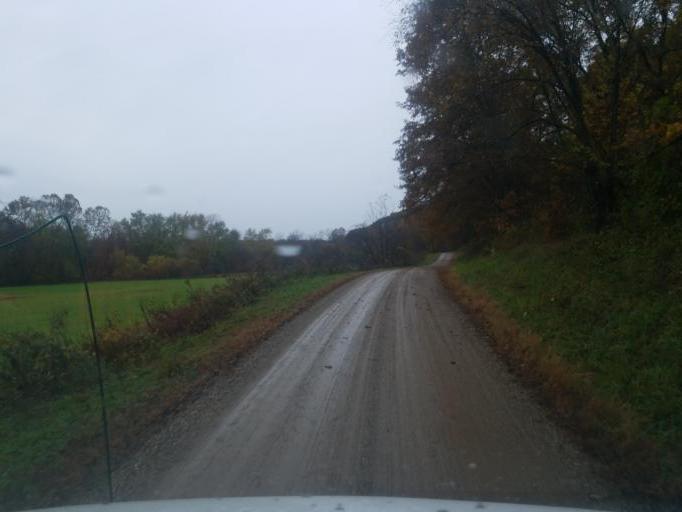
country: US
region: Ohio
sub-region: Washington County
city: Beverly
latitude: 39.4578
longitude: -81.7727
